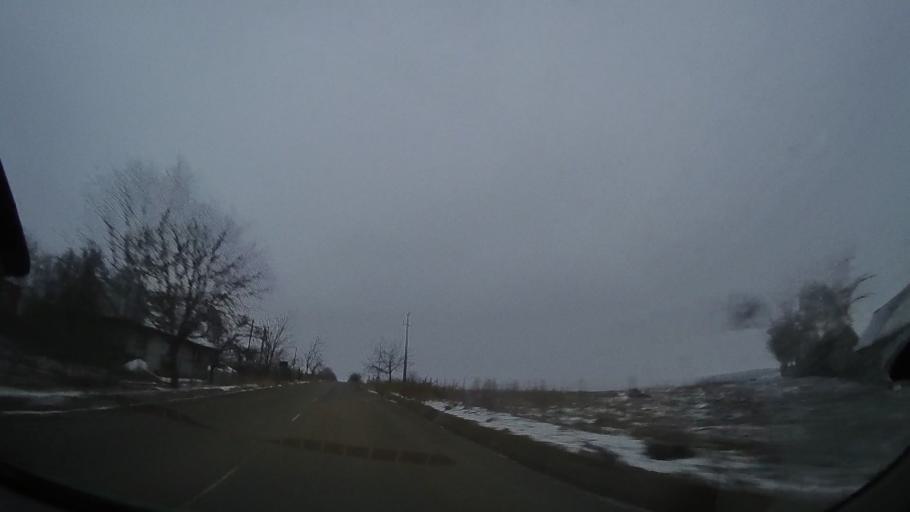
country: RO
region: Vaslui
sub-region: Comuna Gagesti
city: Gagesti
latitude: 46.3950
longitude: 27.9803
